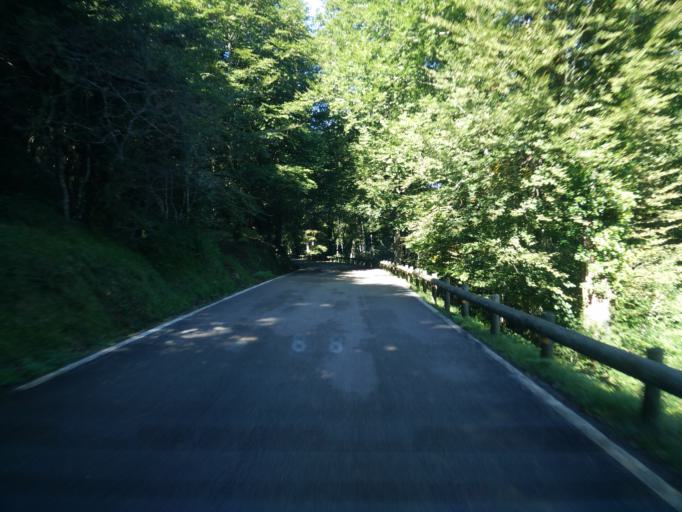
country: ES
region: Cantabria
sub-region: Provincia de Cantabria
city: Ruente
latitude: 43.1069
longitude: -4.2800
